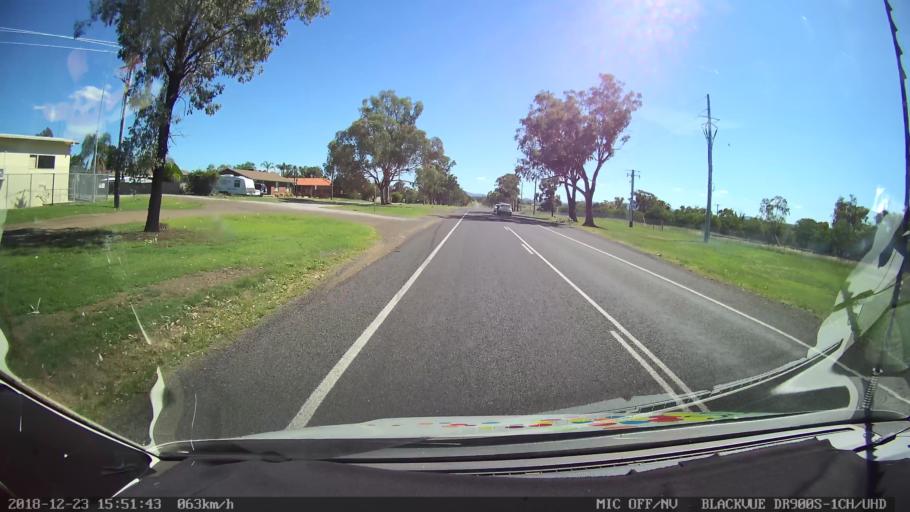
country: AU
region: New South Wales
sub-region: Tamworth Municipality
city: South Tamworth
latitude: -31.1148
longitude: 150.8944
